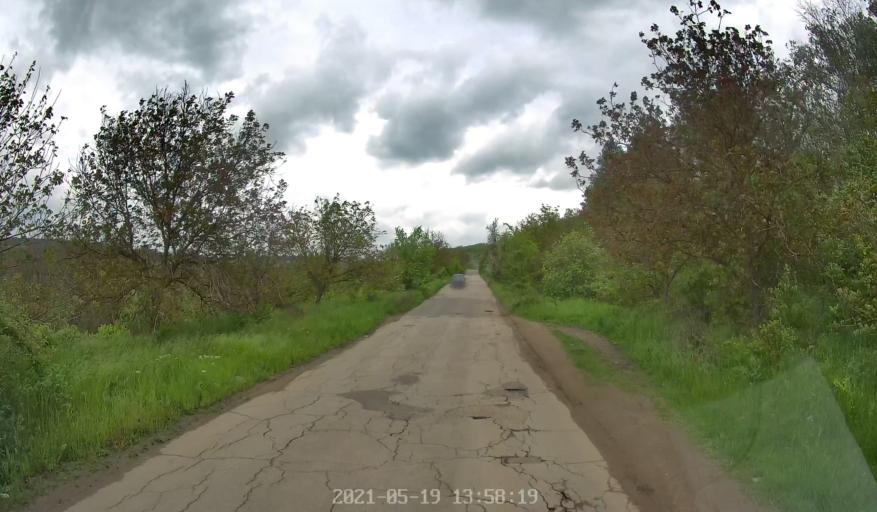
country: MD
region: Chisinau
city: Chisinau
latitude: 47.0421
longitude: 28.9154
